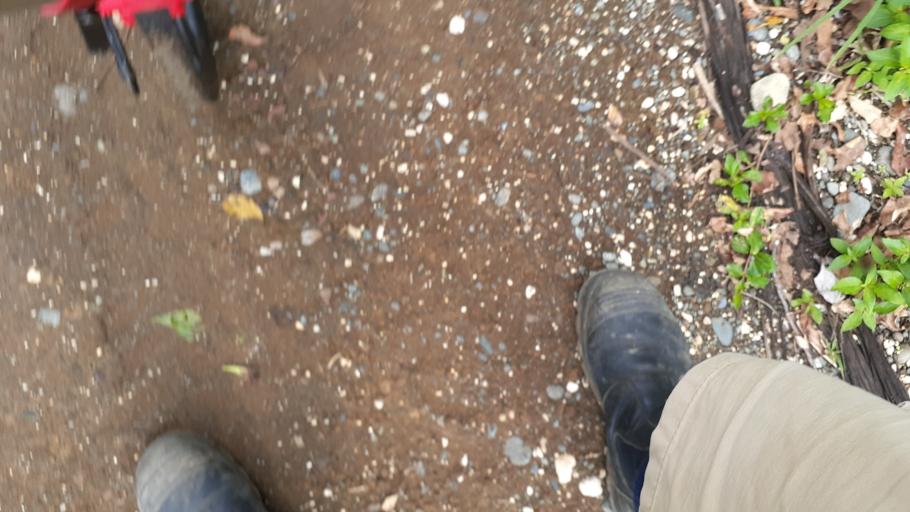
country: VU
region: Penama
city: Saratamata
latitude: -15.9361
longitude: 168.1930
